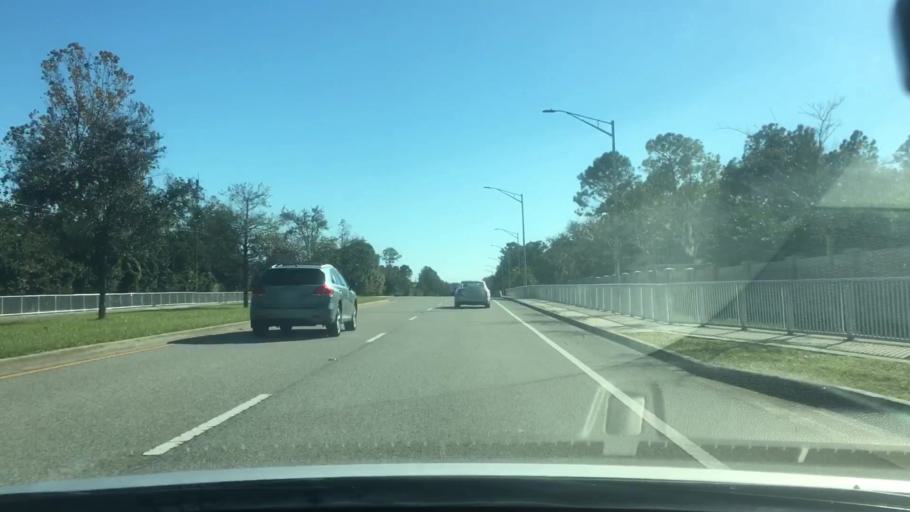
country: US
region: Florida
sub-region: Duval County
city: Neptune Beach
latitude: 30.3075
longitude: -81.4593
